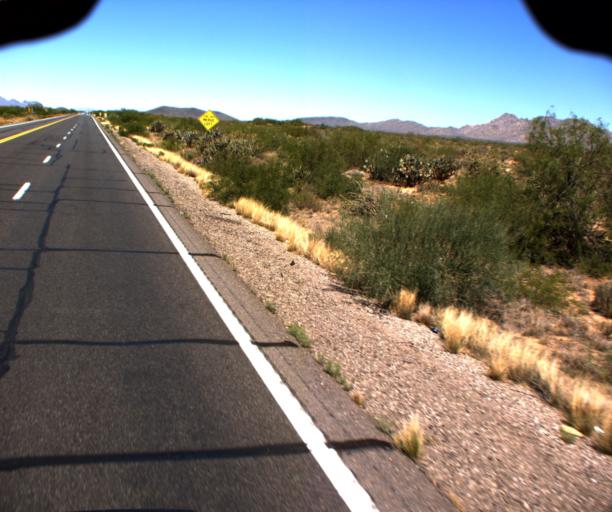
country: US
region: Arizona
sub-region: Yavapai County
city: Congress
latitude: 34.1367
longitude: -112.9696
